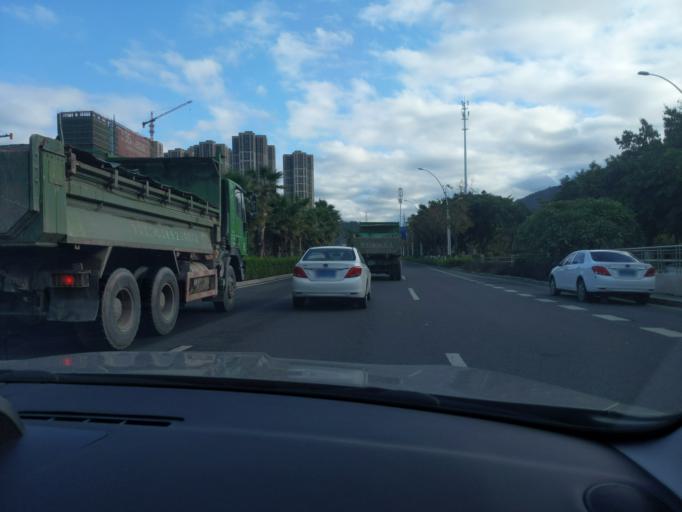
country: CN
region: Fujian
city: Houxi
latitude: 24.6339
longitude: 118.0715
